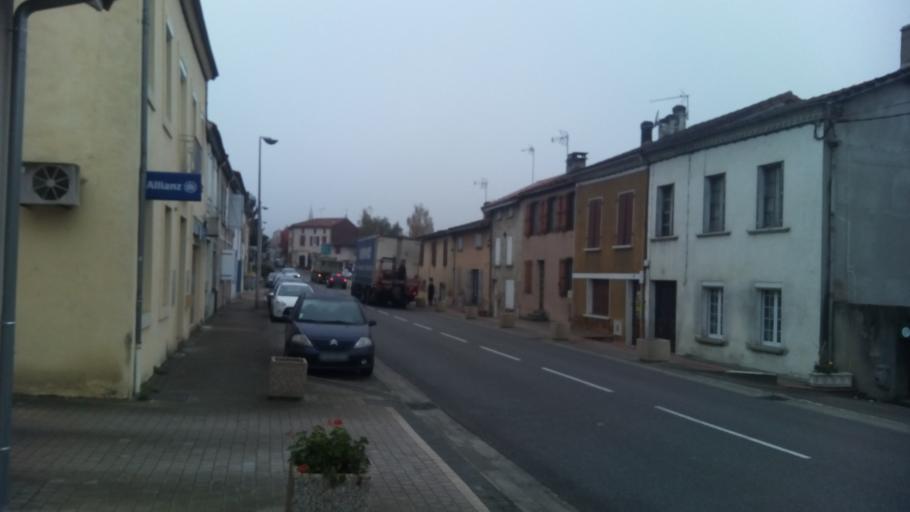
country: FR
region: Midi-Pyrenees
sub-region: Departement du Gers
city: Nogaro
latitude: 43.7612
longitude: -0.0307
